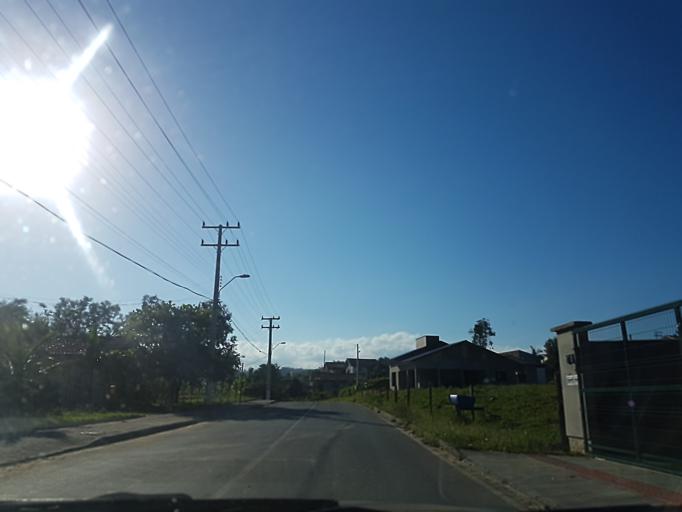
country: BR
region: Santa Catarina
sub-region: Braco Do Norte
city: Braco do Norte
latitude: -28.3300
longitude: -49.1648
